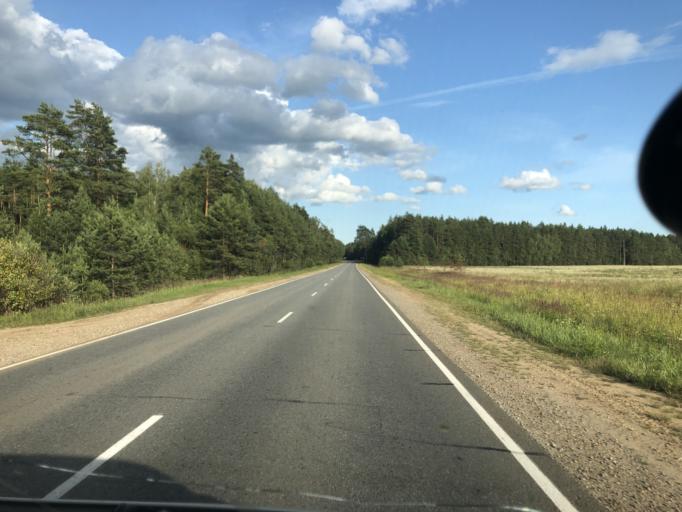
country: RU
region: Kaluga
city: Yukhnov
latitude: 54.7168
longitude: 35.2321
